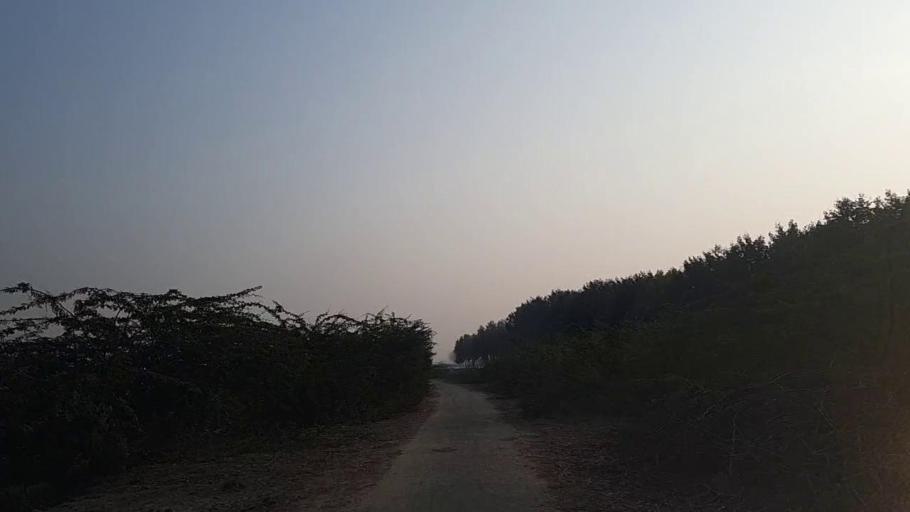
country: PK
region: Sindh
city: Nawabshah
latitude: 26.2378
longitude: 68.4711
